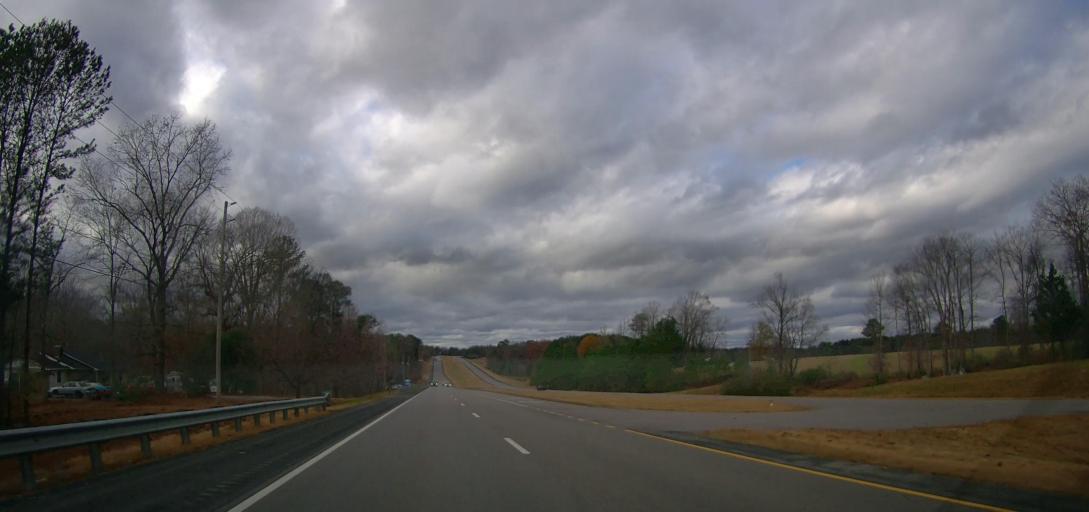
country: US
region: Alabama
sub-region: Morgan County
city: Falkville
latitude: 34.2551
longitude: -86.9758
